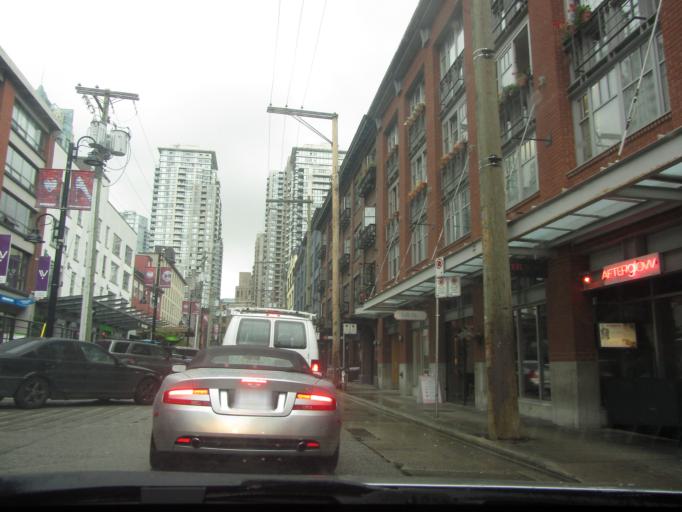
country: CA
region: British Columbia
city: West End
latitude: 49.2762
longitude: -123.1208
